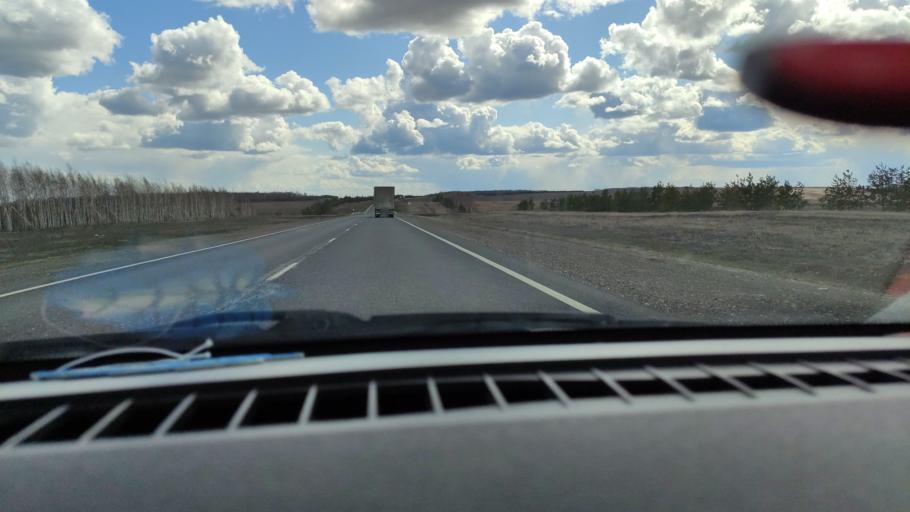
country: RU
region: Samara
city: Syzran'
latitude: 52.8853
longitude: 48.2935
